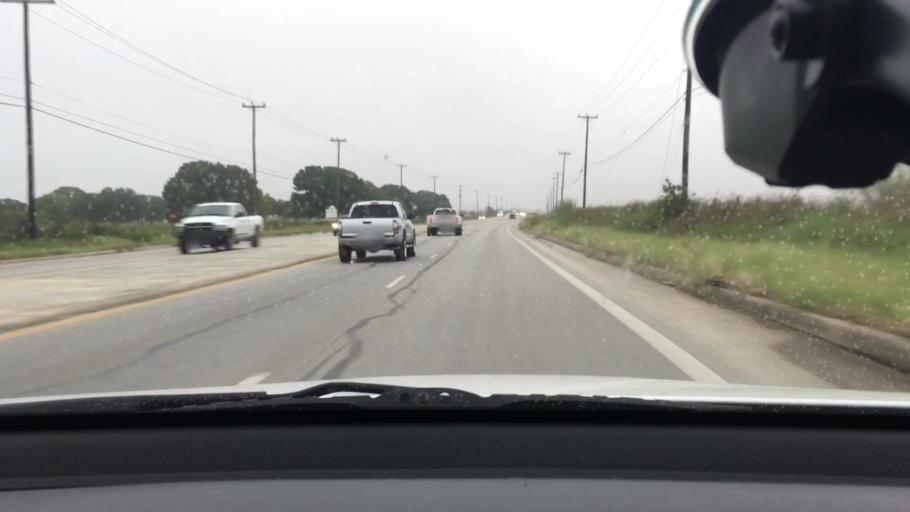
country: US
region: Texas
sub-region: Bexar County
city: Live Oak
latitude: 29.5983
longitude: -98.3394
